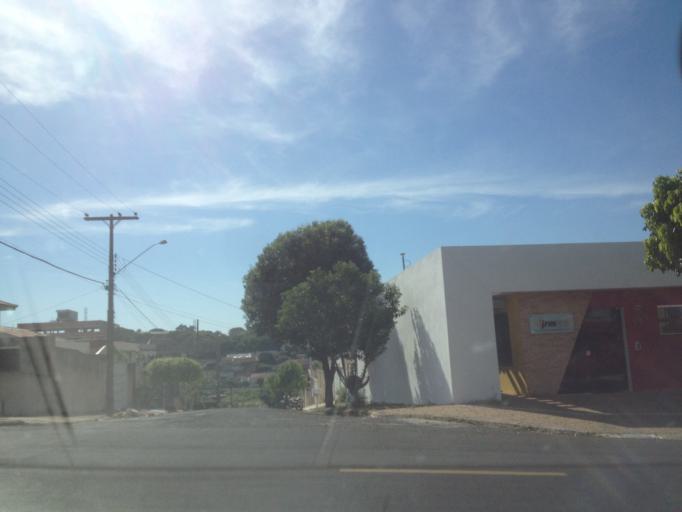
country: BR
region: Sao Paulo
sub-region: Marilia
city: Marilia
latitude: -22.2262
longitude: -49.9457
